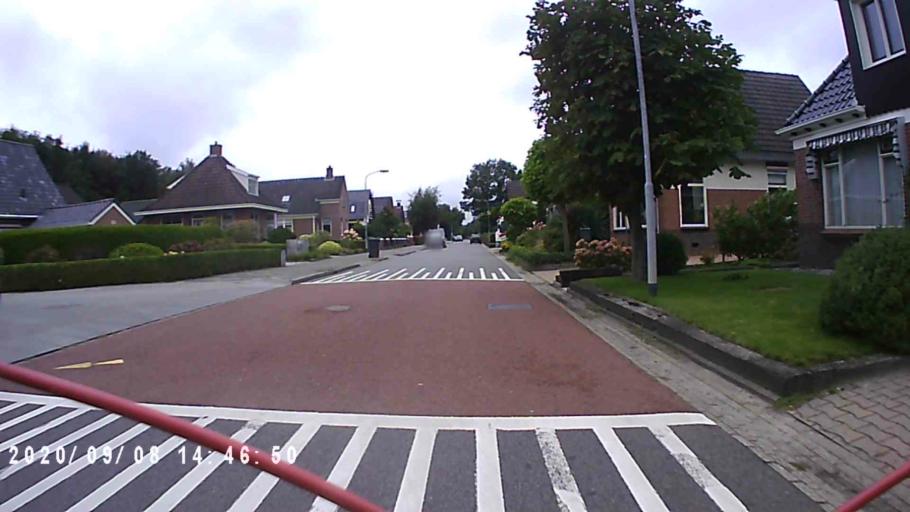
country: NL
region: Groningen
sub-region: Gemeente Slochteren
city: Slochteren
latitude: 53.2348
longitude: 6.8137
